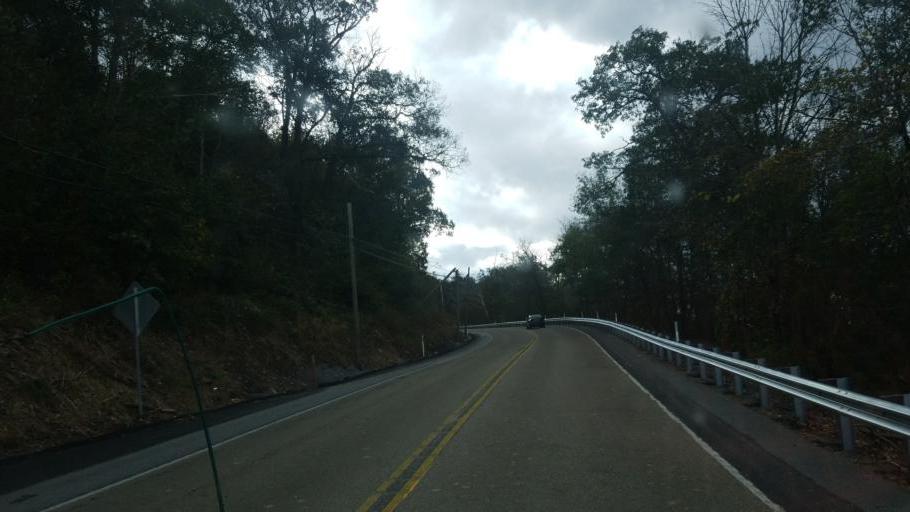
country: US
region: Pennsylvania
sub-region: Fulton County
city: McConnellsburg
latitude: 39.9208
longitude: -77.9584
